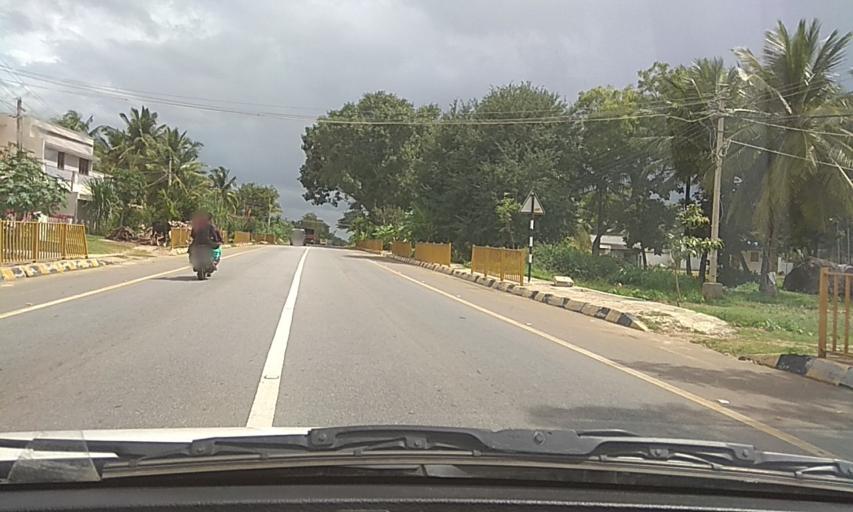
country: IN
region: Karnataka
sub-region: Tumkur
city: Kunigal
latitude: 13.0606
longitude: 77.0267
